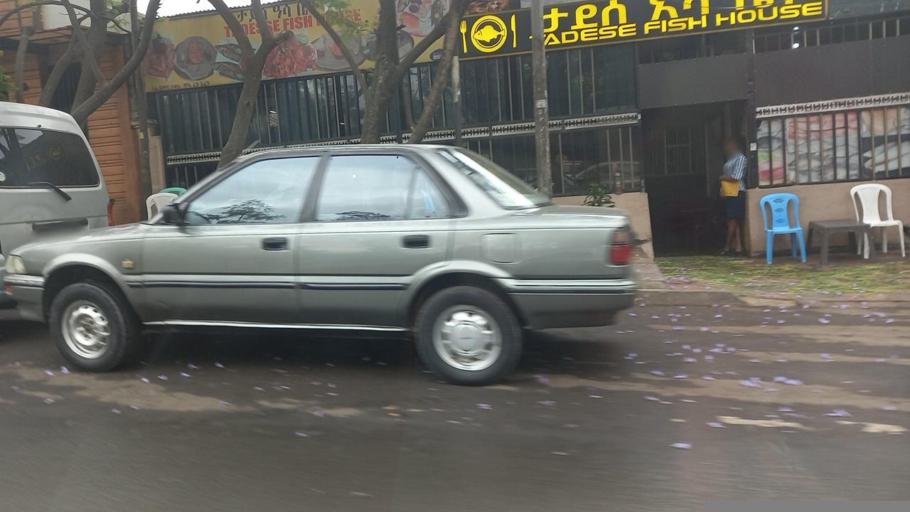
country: ET
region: Adis Abeba
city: Addis Ababa
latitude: 9.0040
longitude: 38.8173
